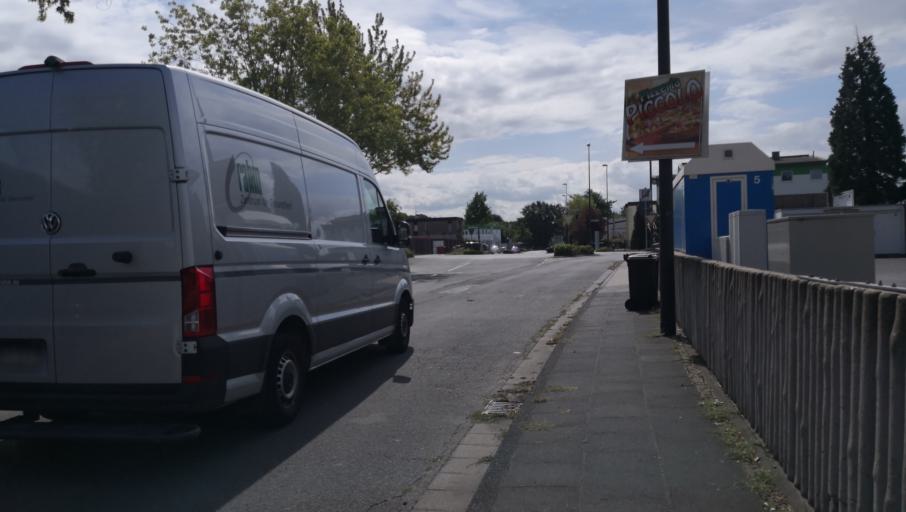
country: DE
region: North Rhine-Westphalia
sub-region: Regierungsbezirk Koln
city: Wahn-Heide
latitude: 50.8385
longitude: 7.1136
